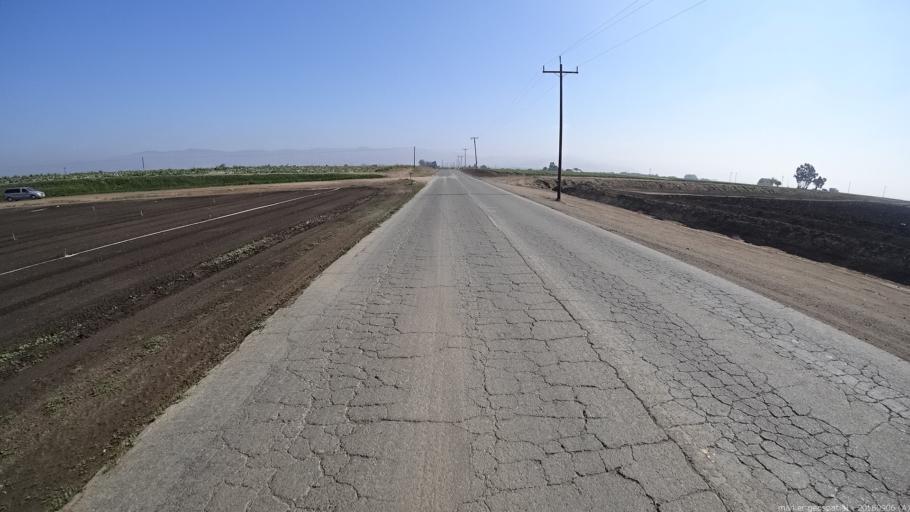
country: US
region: California
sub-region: Monterey County
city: Chualar
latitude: 36.5615
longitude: -121.5238
